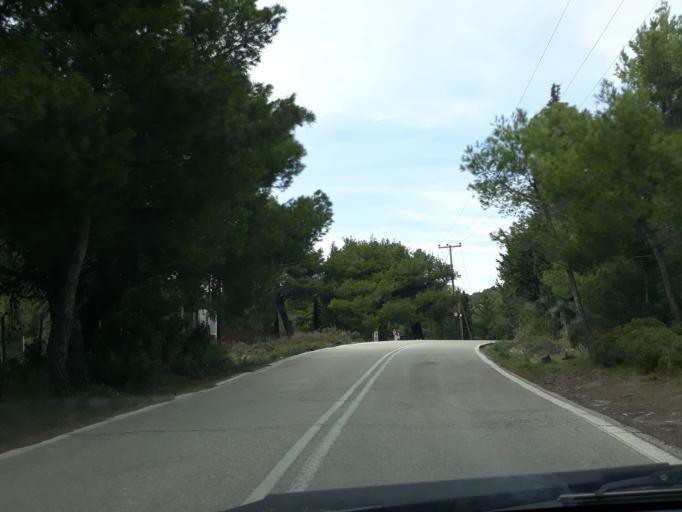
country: GR
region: Attica
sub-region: Nomarchia Anatolikis Attikis
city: Varybobi
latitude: 38.1382
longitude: 23.7930
